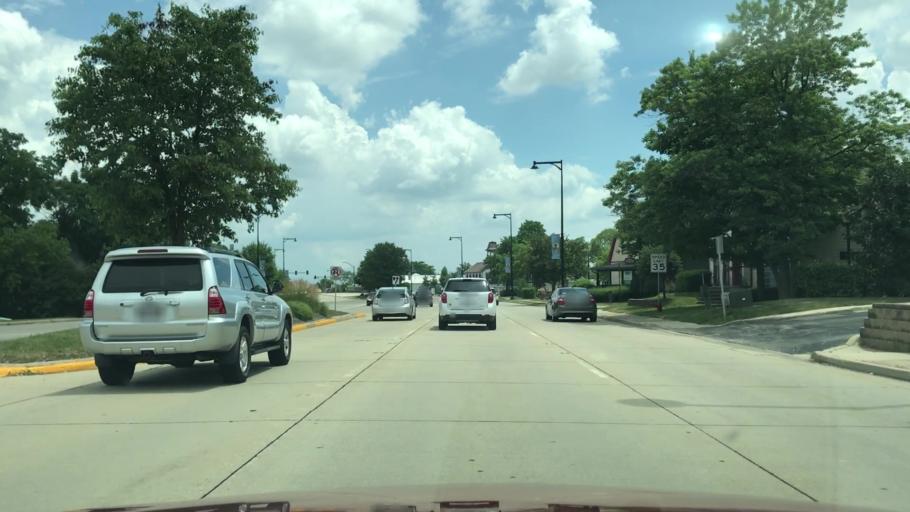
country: US
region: Illinois
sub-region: DuPage County
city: Bloomingdale
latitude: 41.9580
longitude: -88.0849
